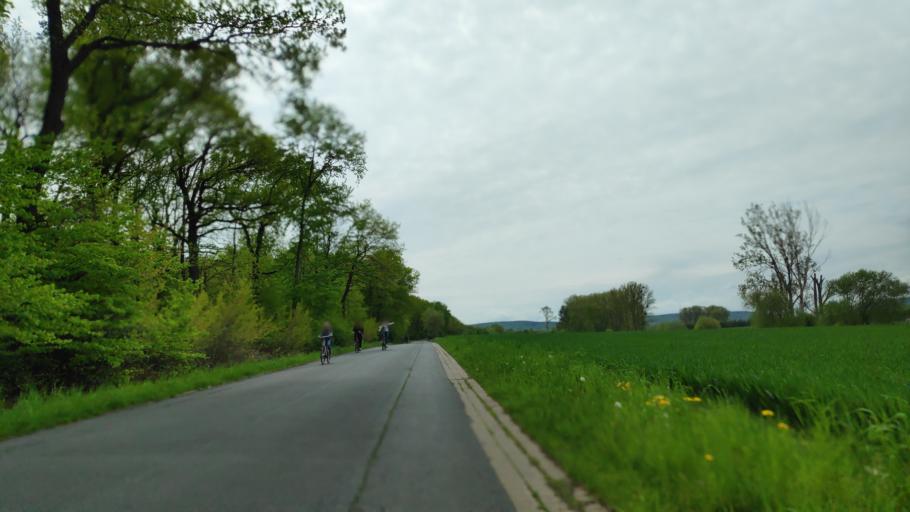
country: DE
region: Lower Saxony
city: Buckeburg
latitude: 52.3035
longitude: 8.9922
